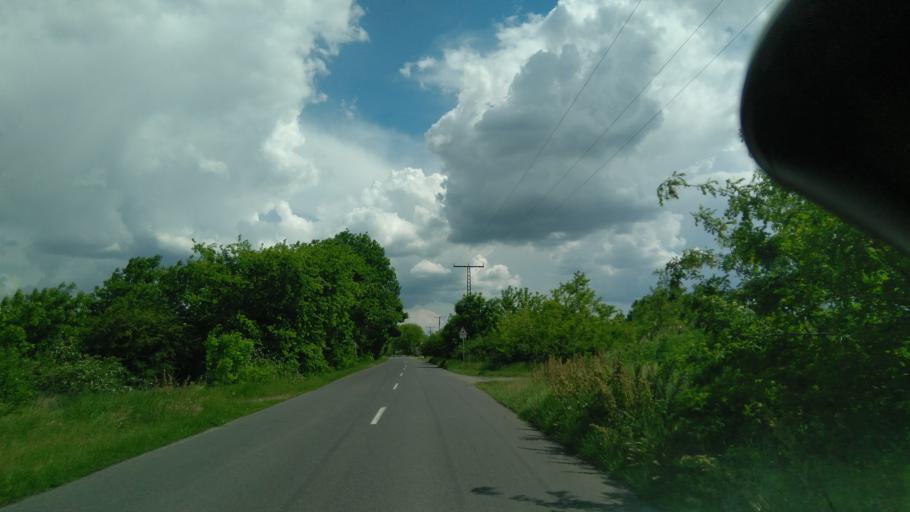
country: HU
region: Bekes
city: Korosladany
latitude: 46.9770
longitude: 21.0568
